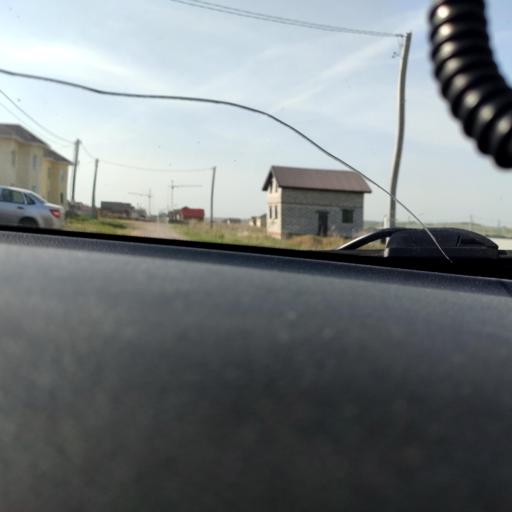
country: RU
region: Tatarstan
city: Stolbishchi
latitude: 55.7220
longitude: 49.3366
